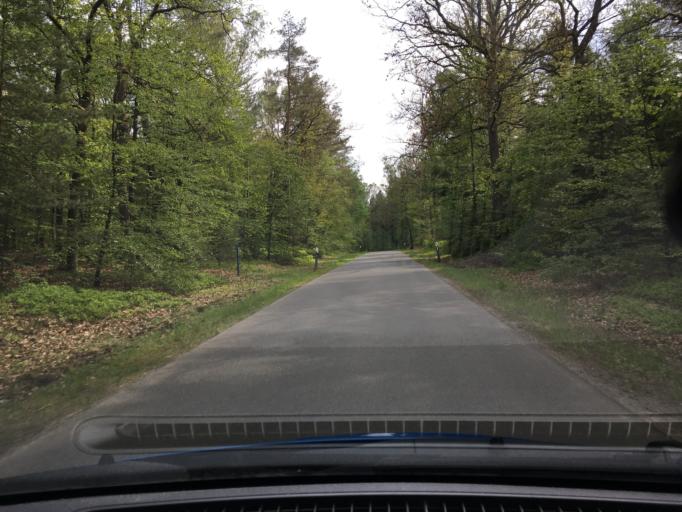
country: DE
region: Lower Saxony
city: Eimke
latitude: 52.9797
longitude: 10.2501
